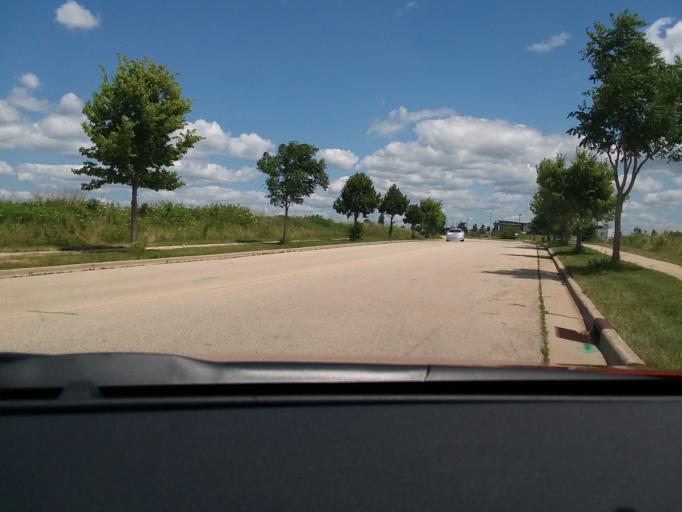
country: US
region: Wisconsin
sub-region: Dane County
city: Windsor
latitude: 43.1961
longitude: -89.3304
